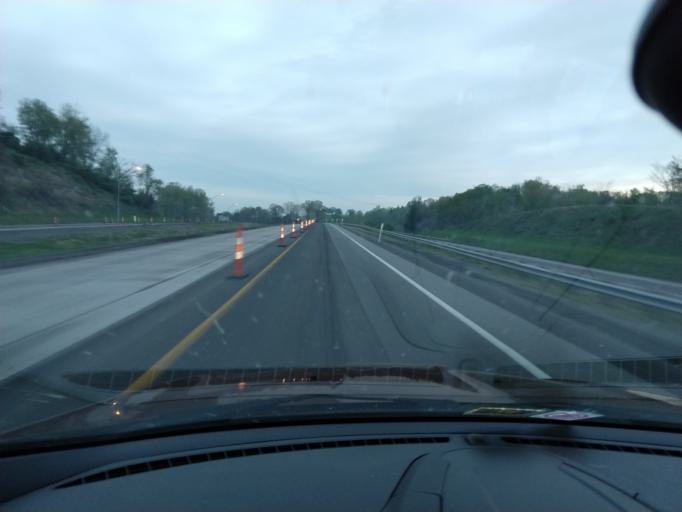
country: US
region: West Virginia
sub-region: Braxton County
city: Sutton
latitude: 38.7053
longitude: -80.6611
